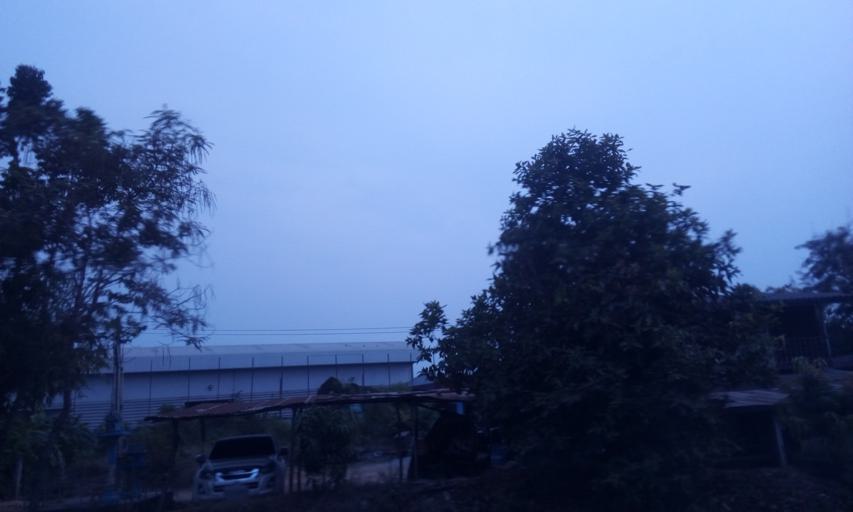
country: TH
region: Chachoengsao
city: Plaeng Yao
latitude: 13.5979
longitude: 101.1834
